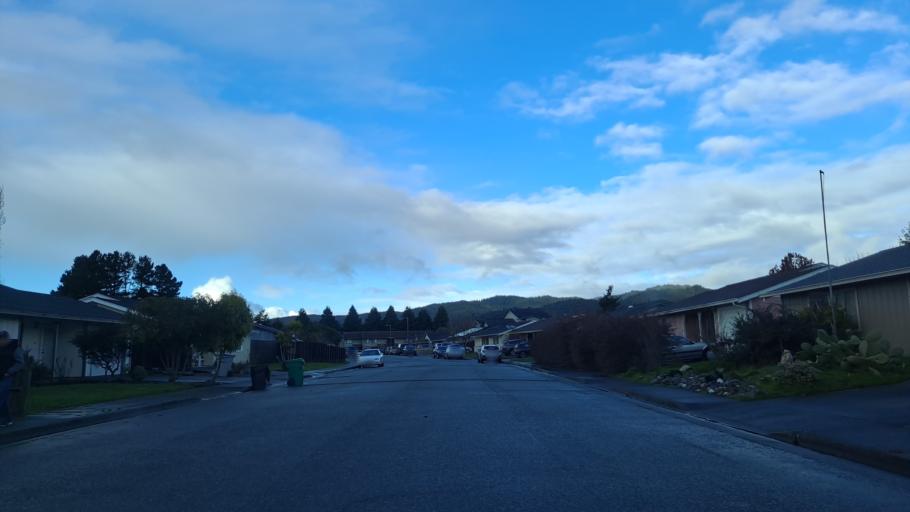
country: US
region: California
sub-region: Humboldt County
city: Fortuna
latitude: 40.5830
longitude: -124.1410
